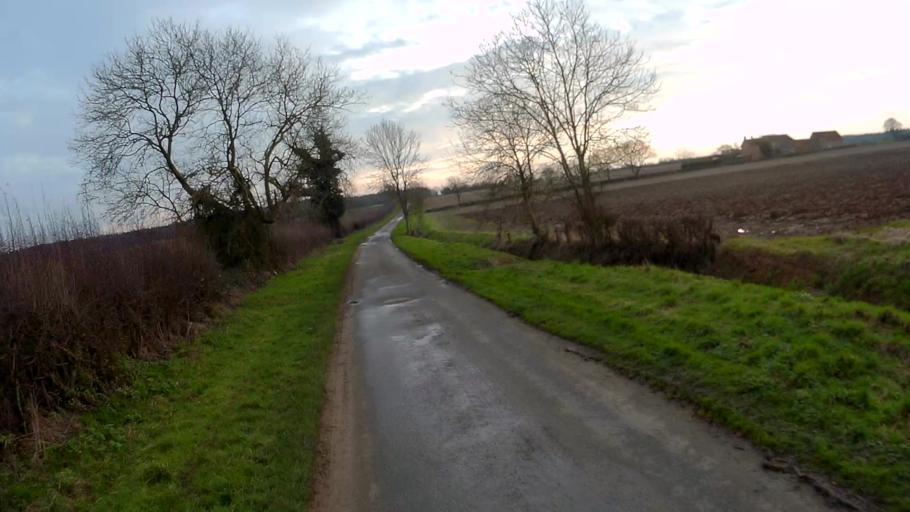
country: GB
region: England
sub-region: Lincolnshire
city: Bourne
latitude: 52.8279
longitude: -0.4054
